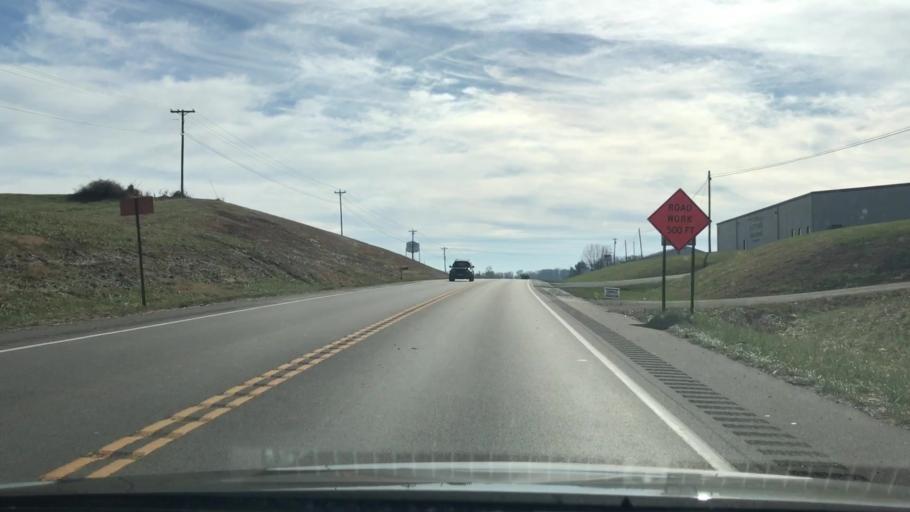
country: US
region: Kentucky
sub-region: Monroe County
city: Tompkinsville
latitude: 36.7328
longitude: -85.6876
